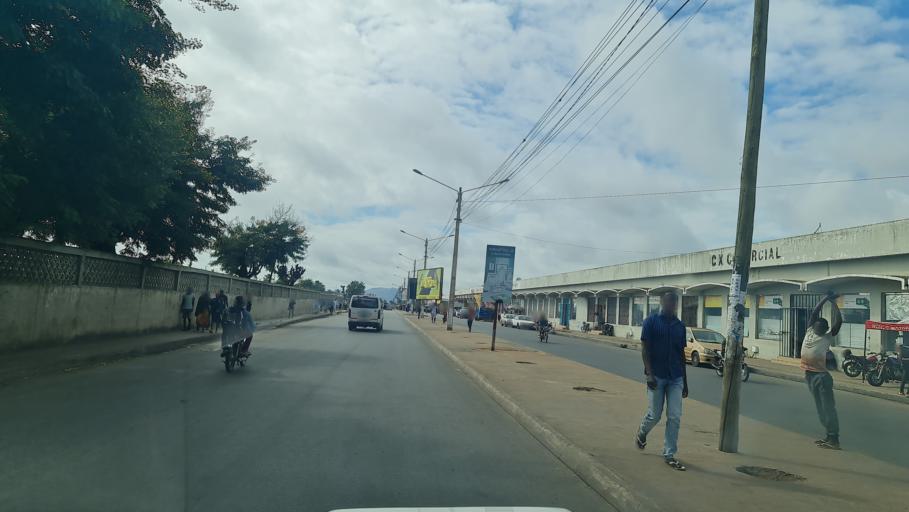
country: MZ
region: Nampula
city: Nampula
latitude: -15.1142
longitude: 39.2705
